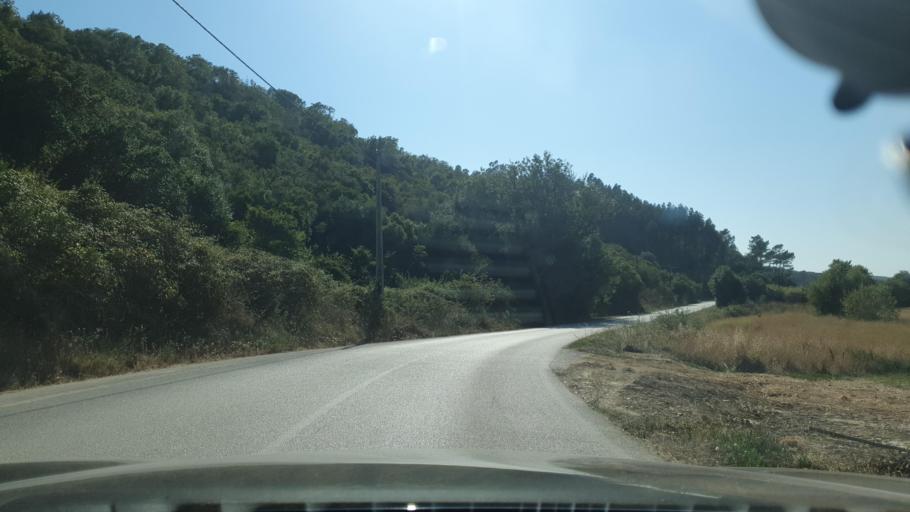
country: PT
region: Beja
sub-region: Odemira
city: Sao Teotonio
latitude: 37.4308
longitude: -8.7766
